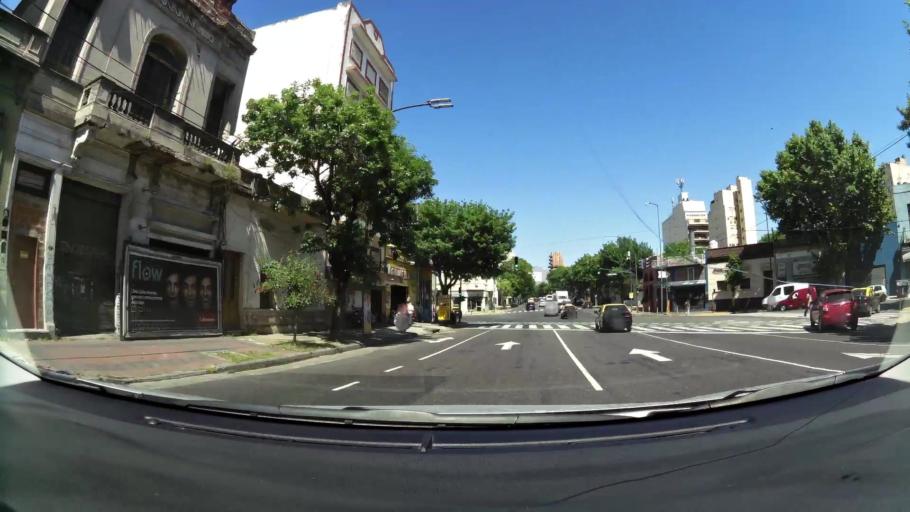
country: AR
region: Buenos Aires F.D.
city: Buenos Aires
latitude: -34.6292
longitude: -58.4051
